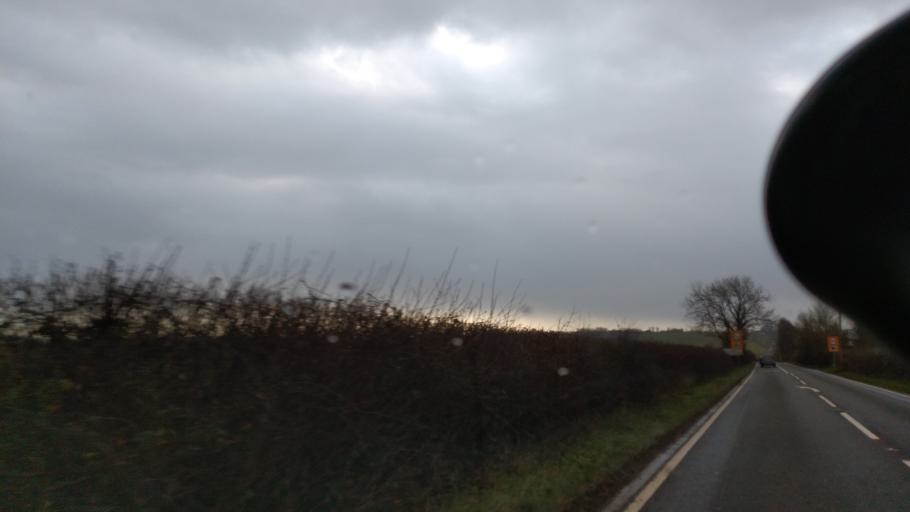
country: GB
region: England
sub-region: Somerset
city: Shepton Mallet
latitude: 51.1590
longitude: -2.5416
